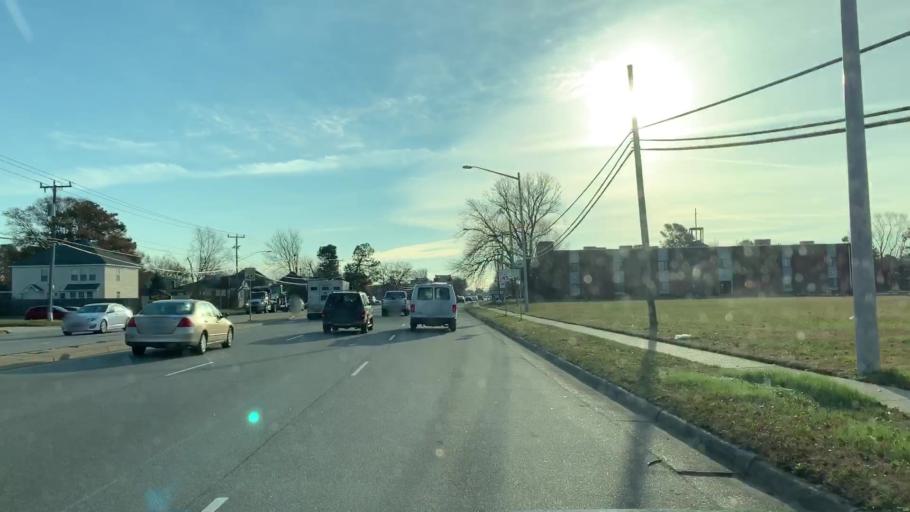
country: US
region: Virginia
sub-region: City of Chesapeake
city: Chesapeake
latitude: 36.8030
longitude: -76.1864
